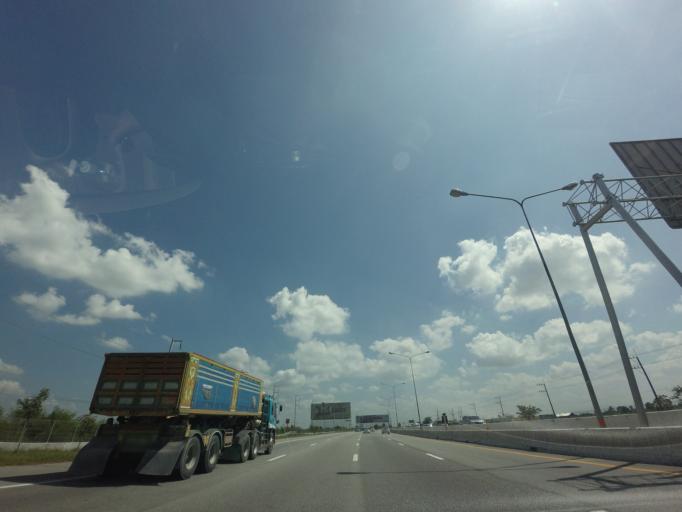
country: TH
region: Chachoengsao
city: Bang Pakong
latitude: 13.5935
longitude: 100.9628
